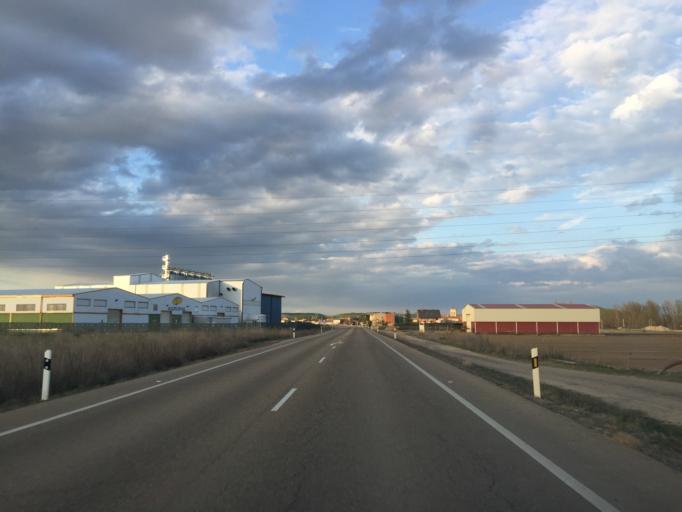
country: ES
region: Castille and Leon
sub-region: Provincia de Palencia
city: Soto de Cerrato
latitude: 41.9765
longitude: -4.4353
